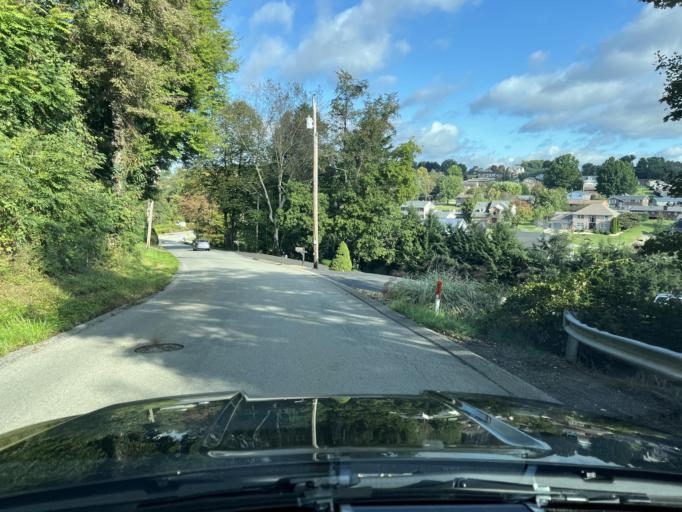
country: US
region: Pennsylvania
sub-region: Fayette County
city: South Uniontown
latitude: 39.8907
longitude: -79.7566
